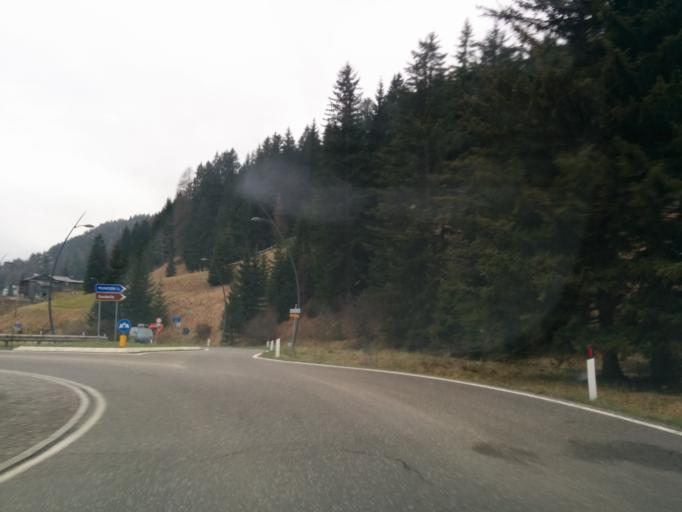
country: IT
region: Trentino-Alto Adige
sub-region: Provincia di Trento
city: Mazzin
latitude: 46.4475
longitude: 11.6967
